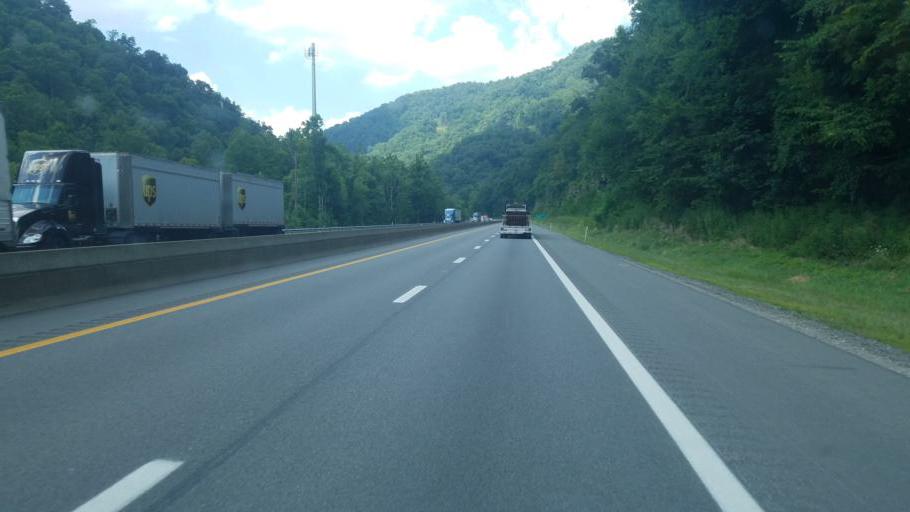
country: US
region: West Virginia
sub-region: Kanawha County
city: Montgomery
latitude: 38.0386
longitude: -81.3627
